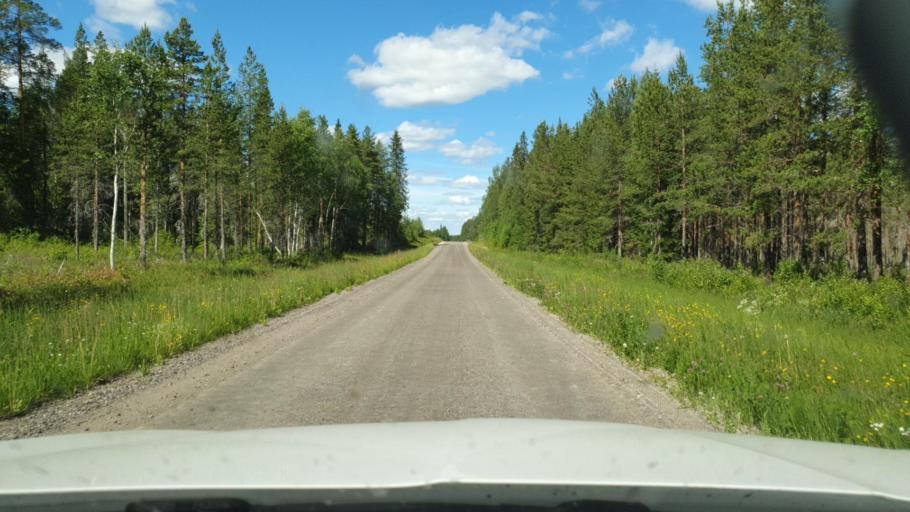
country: SE
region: Vaesterbotten
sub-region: Skelleftea Kommun
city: Byske
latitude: 65.1404
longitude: 21.1809
